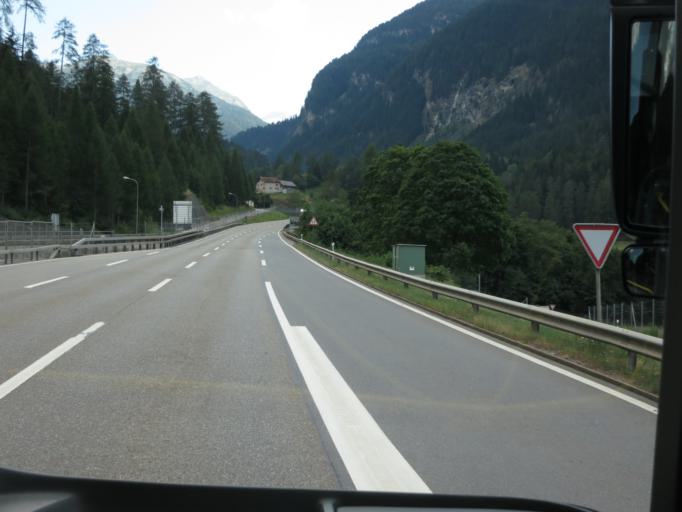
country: CH
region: Grisons
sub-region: Hinterrhein District
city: Thusis
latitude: 46.5985
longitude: 9.4306
